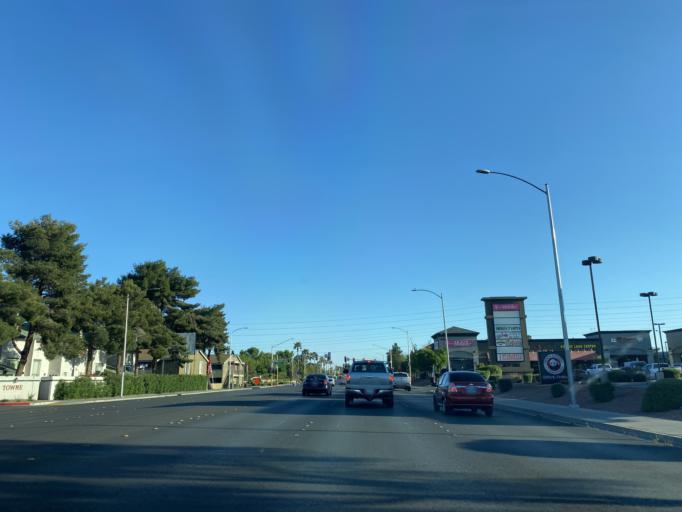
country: US
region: Nevada
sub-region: Clark County
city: Winchester
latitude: 36.1421
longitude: -115.1188
